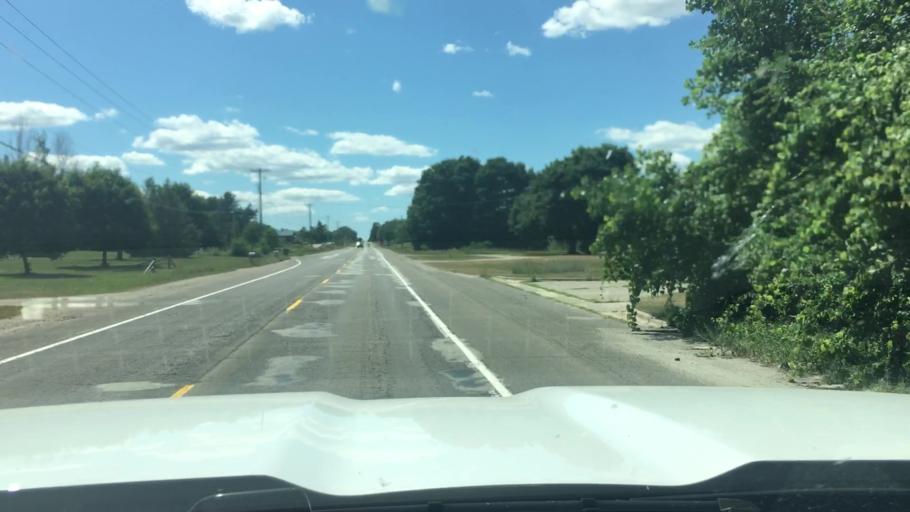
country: US
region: Michigan
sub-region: Kent County
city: Rockford
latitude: 43.1608
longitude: -85.6183
